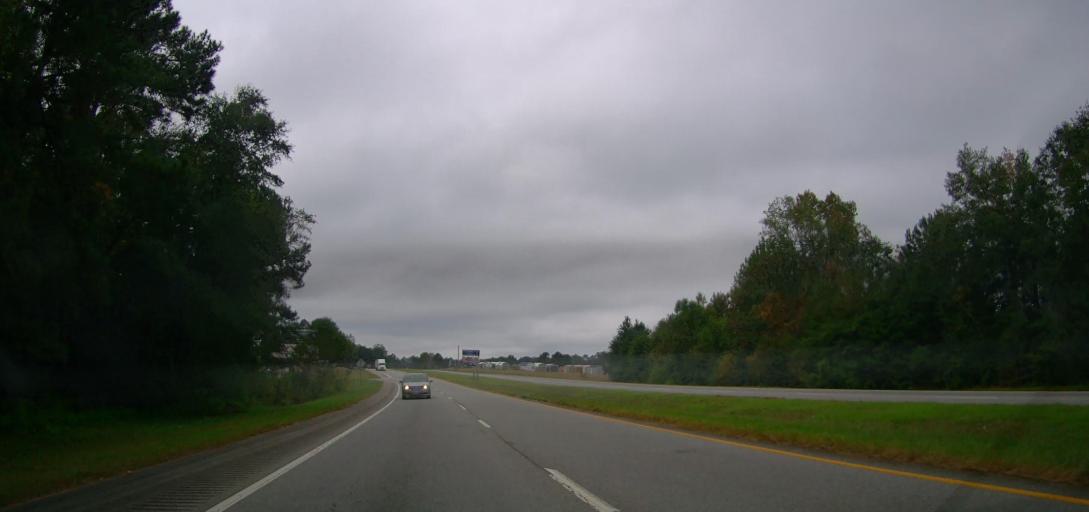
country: US
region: Georgia
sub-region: Thomas County
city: Thomasville
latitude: 30.8711
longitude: -83.9929
